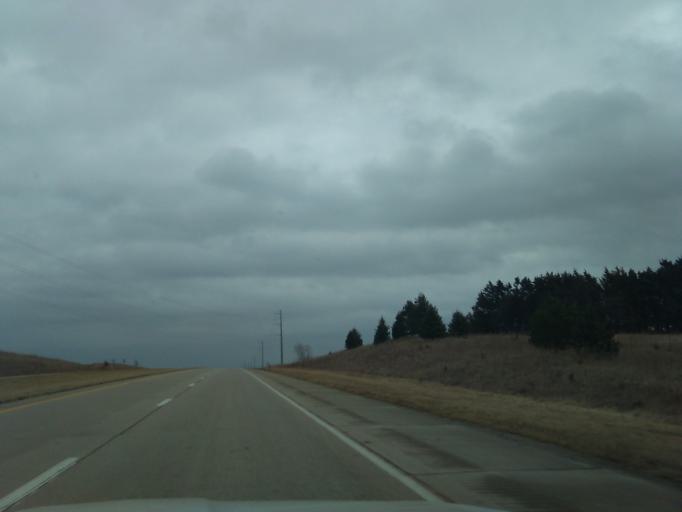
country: US
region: Nebraska
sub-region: Otoe County
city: Syracuse
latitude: 40.6700
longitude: -96.1047
